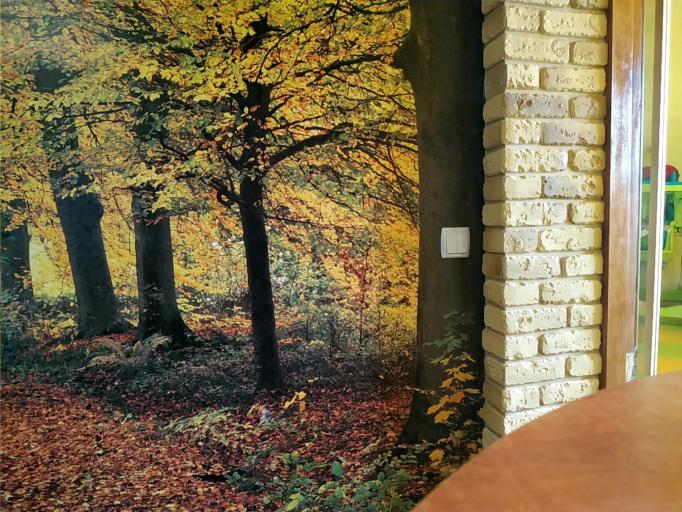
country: RU
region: Vologda
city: Nelazskoye
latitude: 59.4119
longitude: 37.6086
